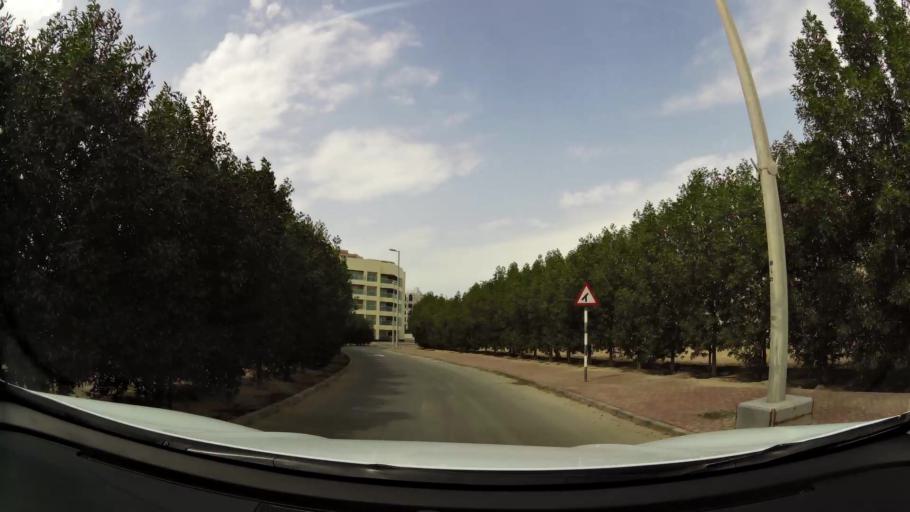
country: AE
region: Abu Dhabi
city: Abu Dhabi
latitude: 24.4173
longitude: 54.4693
